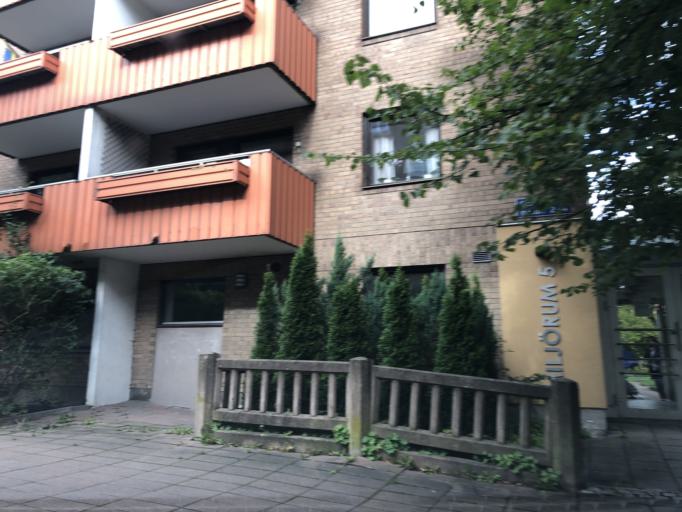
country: SE
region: Vaestra Goetaland
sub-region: Goteborg
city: Goeteborg
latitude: 57.7162
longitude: 11.9983
